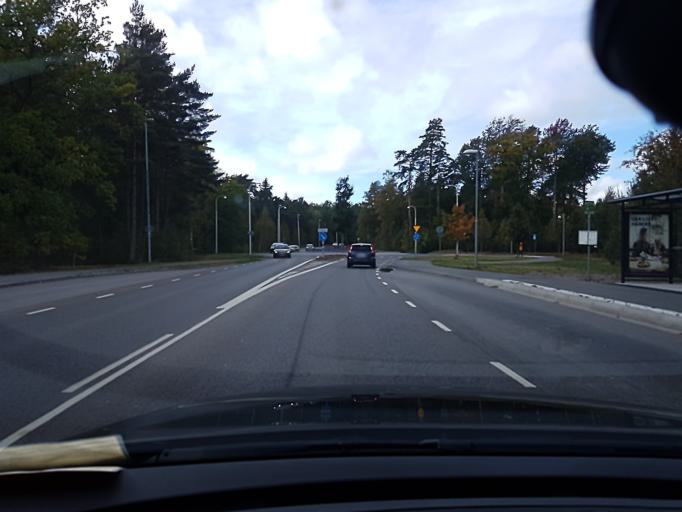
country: SE
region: Kronoberg
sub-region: Vaxjo Kommun
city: Vaexjoe
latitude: 56.8638
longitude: 14.7983
